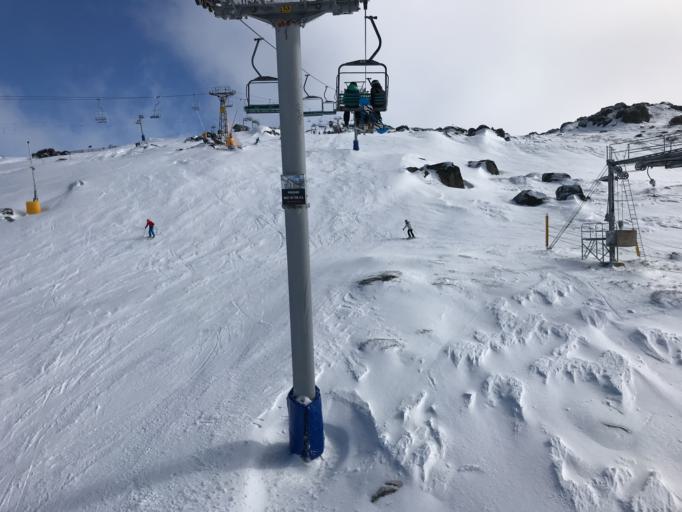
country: AU
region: New South Wales
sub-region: Snowy River
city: Jindabyne
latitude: -36.4094
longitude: 148.3908
